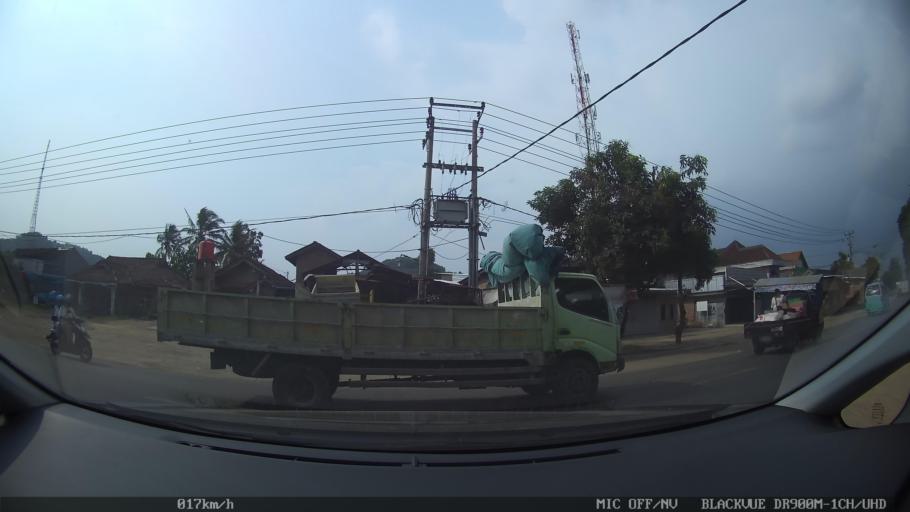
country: ID
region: Lampung
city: Gadingrejo
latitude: -5.3836
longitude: 105.0180
